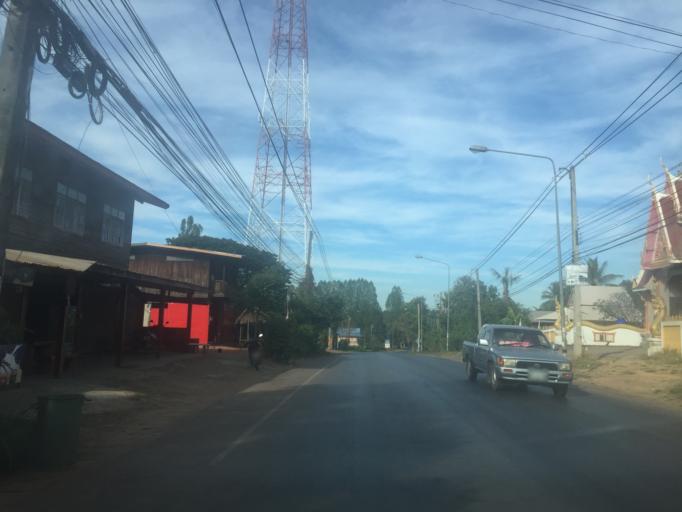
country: TH
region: Changwat Udon Thani
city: Si That
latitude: 16.9745
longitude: 103.2103
